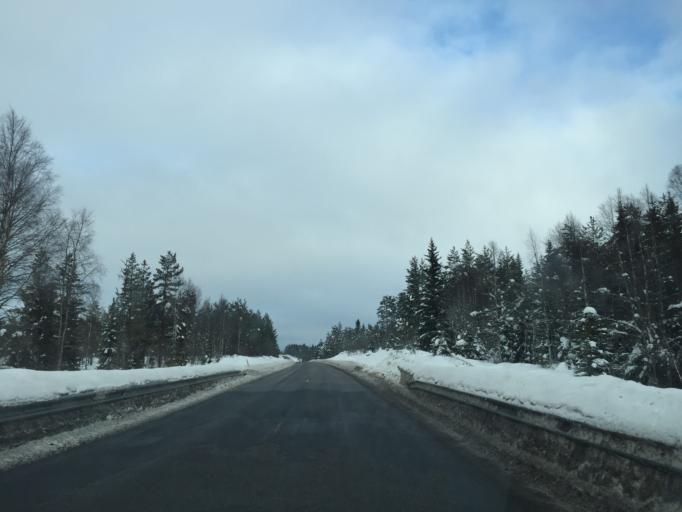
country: NO
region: Hedmark
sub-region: Trysil
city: Innbygda
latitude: 61.1255
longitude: 12.0981
